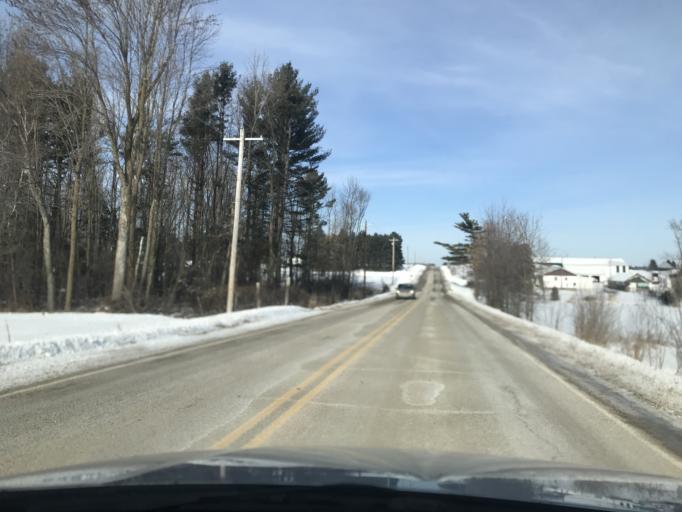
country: US
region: Wisconsin
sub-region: Oconto County
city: Oconto Falls
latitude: 45.1204
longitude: -88.1781
